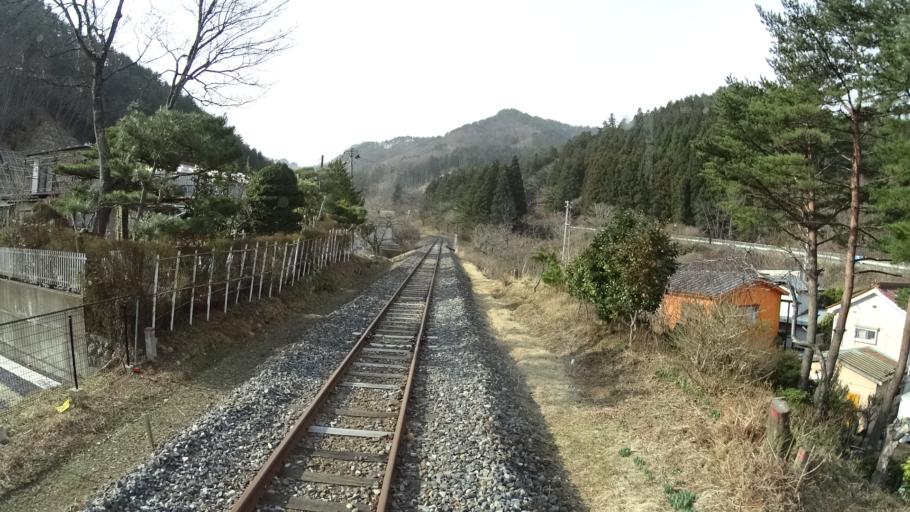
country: JP
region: Iwate
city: Kamaishi
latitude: 39.3202
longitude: 141.8847
